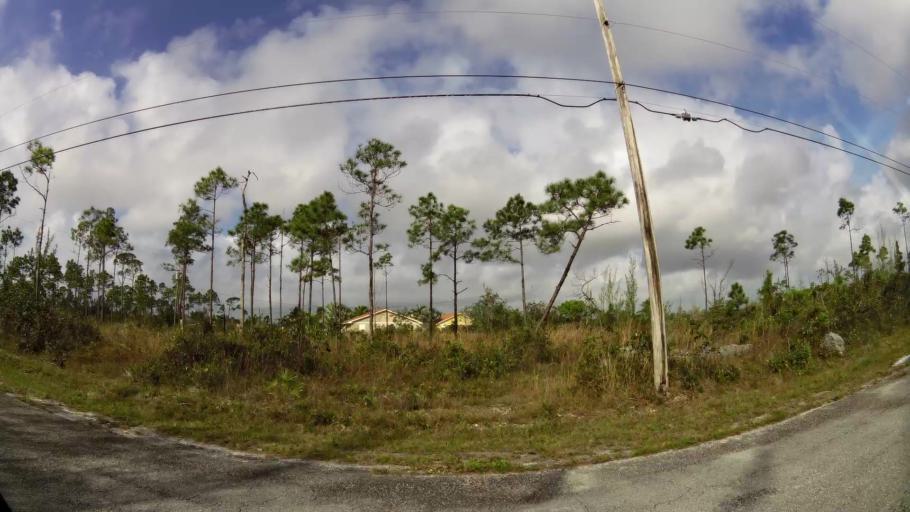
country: BS
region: Freeport
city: Lucaya
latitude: 26.5754
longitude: -78.5886
